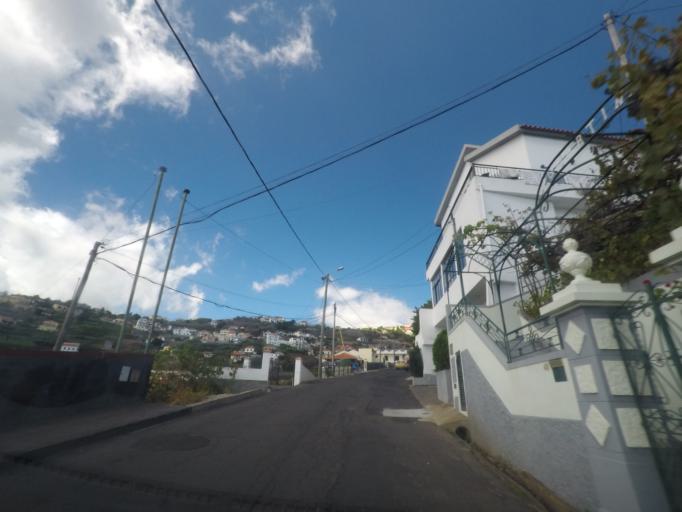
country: PT
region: Madeira
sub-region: Ribeira Brava
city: Campanario
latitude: 32.6698
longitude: -17.0502
